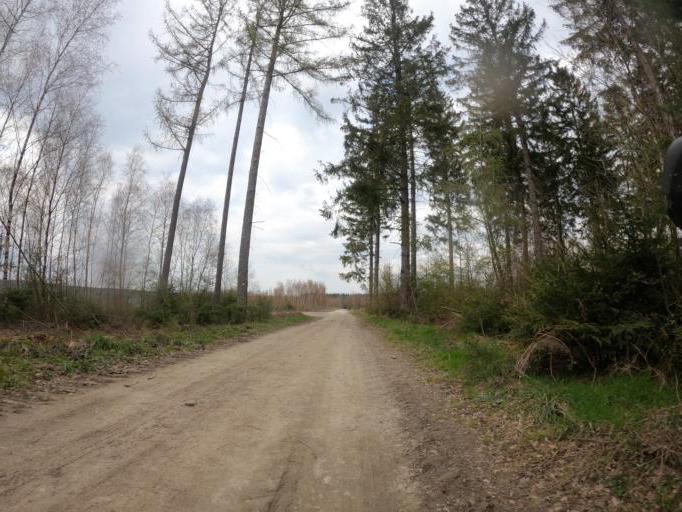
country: DE
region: North Rhine-Westphalia
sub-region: Regierungsbezirk Koln
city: Hurtgenwald
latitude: 50.7084
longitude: 6.3533
